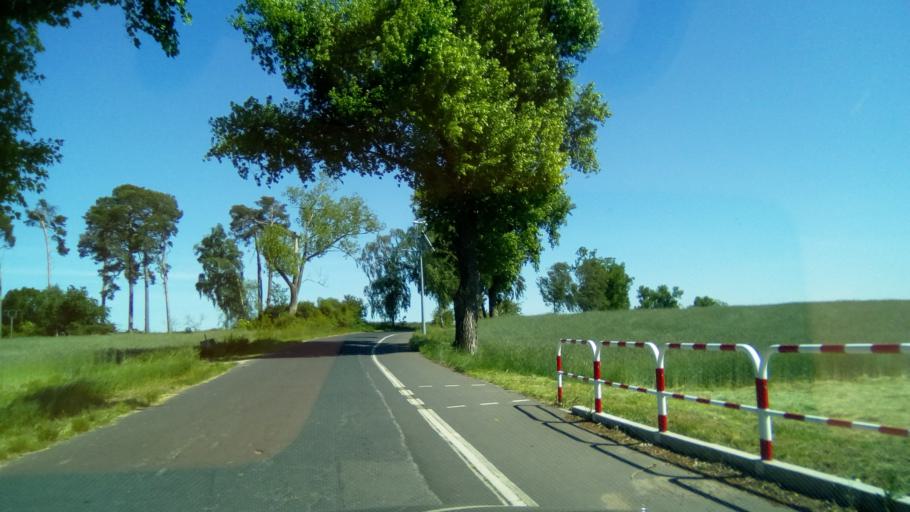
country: PL
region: Greater Poland Voivodeship
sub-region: Powiat gnieznienski
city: Gniezno
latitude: 52.4617
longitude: 17.5641
